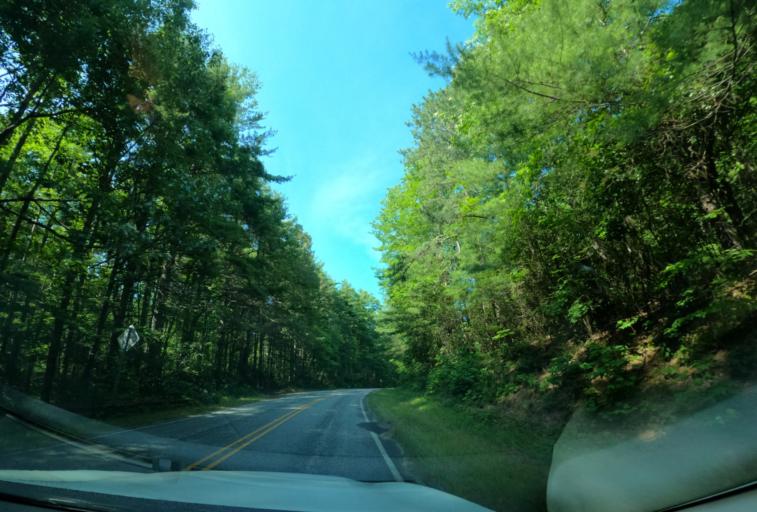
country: US
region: North Carolina
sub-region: Transylvania County
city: Brevard
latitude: 35.1842
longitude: -82.6405
